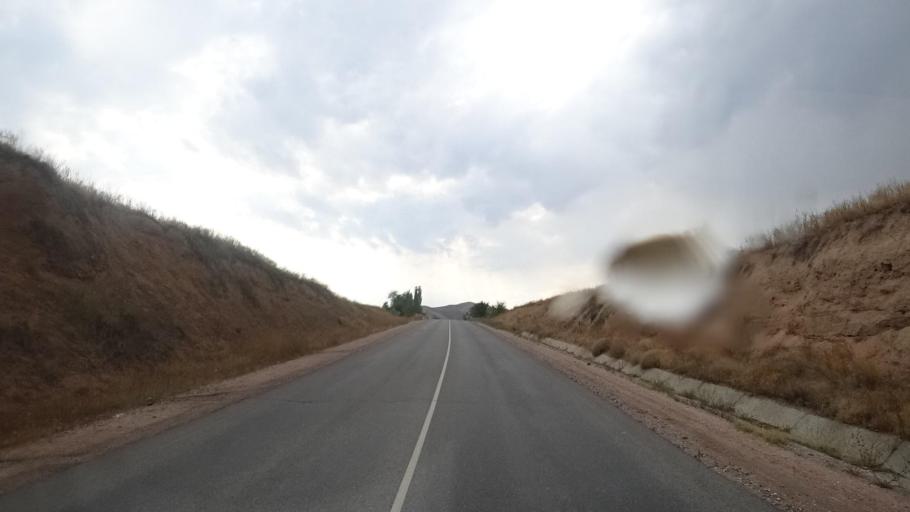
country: KG
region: Jalal-Abad
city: Toktogul
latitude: 41.8574
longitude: 73.0564
